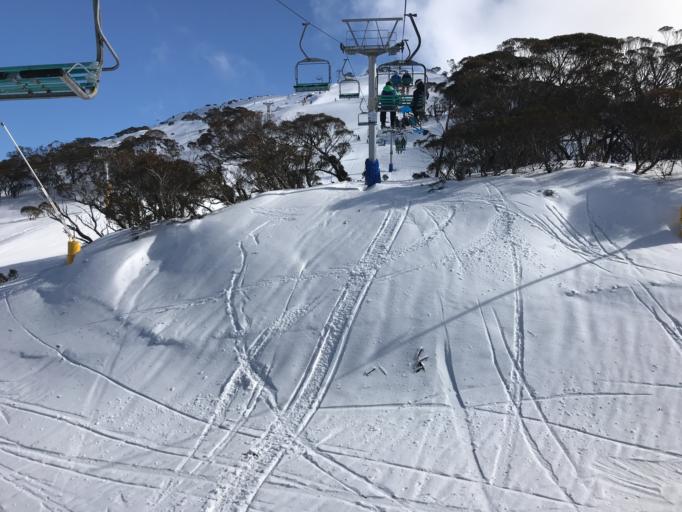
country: AU
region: New South Wales
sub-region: Snowy River
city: Jindabyne
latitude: -36.4100
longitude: 148.3987
